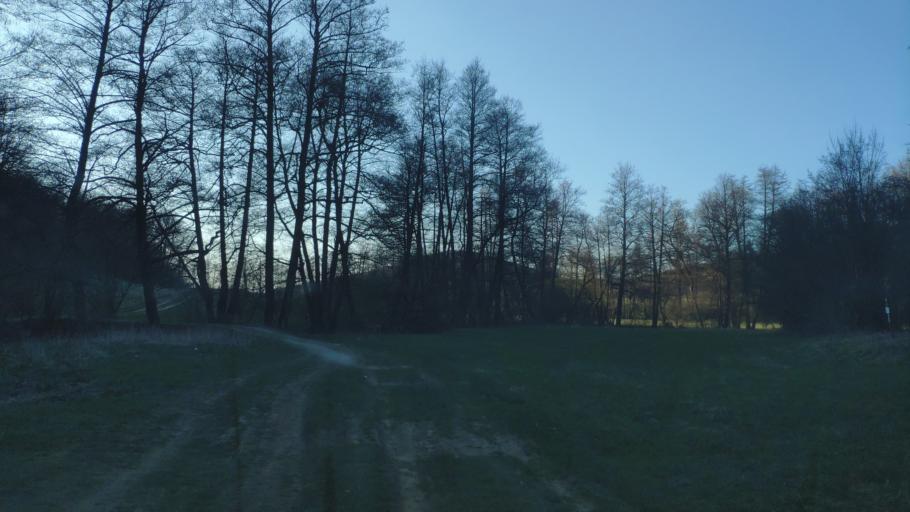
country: HU
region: Borsod-Abauj-Zemplen
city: Putnok
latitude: 48.5163
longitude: 20.3243
